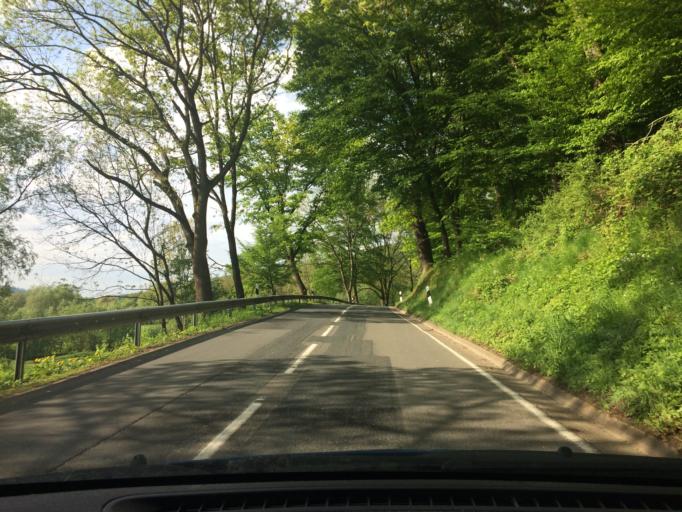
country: DE
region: Lower Saxony
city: Buhren
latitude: 51.5384
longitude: 9.6253
